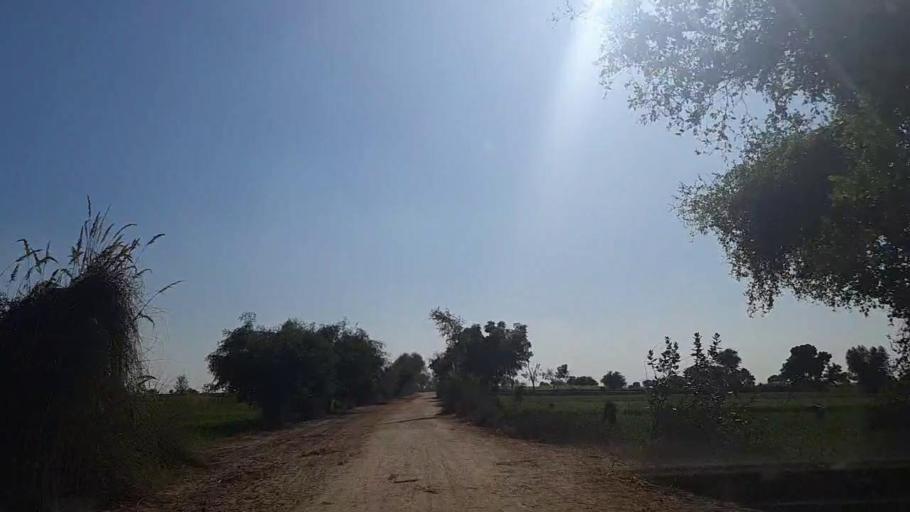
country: PK
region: Sindh
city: Sakrand
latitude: 26.2426
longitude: 68.1999
